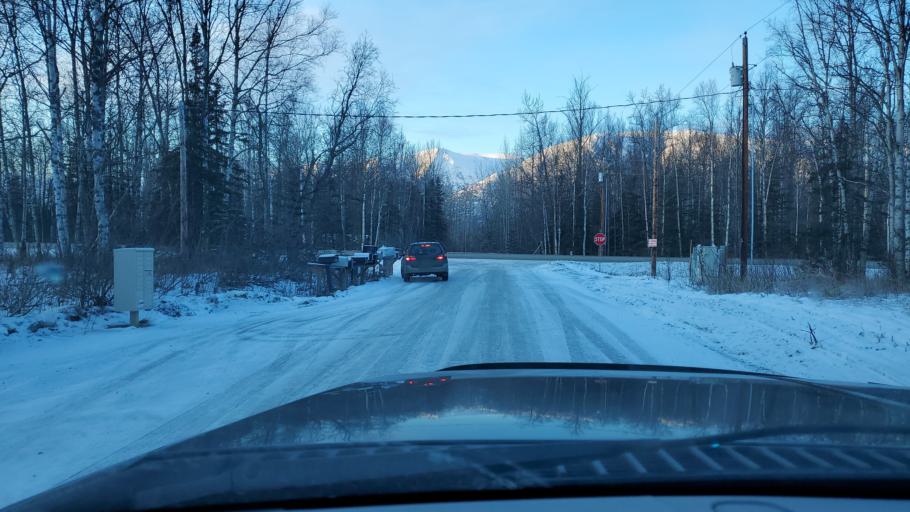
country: US
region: Alaska
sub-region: Matanuska-Susitna Borough
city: Lakes
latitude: 61.6682
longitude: -149.2955
